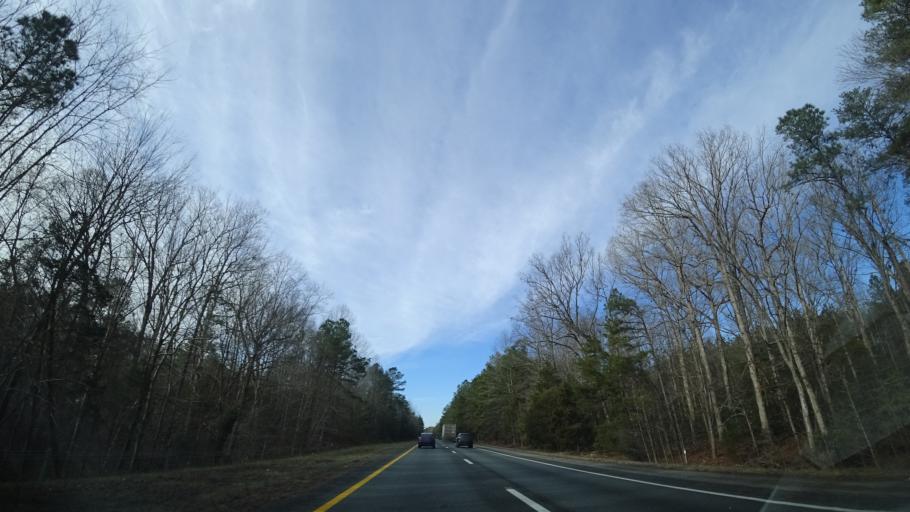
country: US
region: Virginia
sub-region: New Kent County
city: New Kent
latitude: 37.4845
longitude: -76.9555
